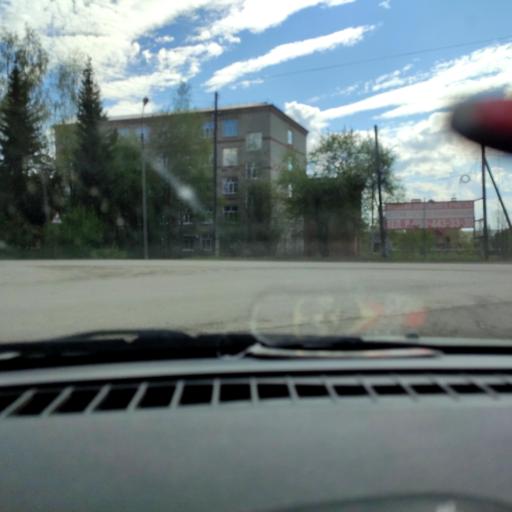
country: RU
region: Perm
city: Kudymkar
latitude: 59.0186
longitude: 54.6492
